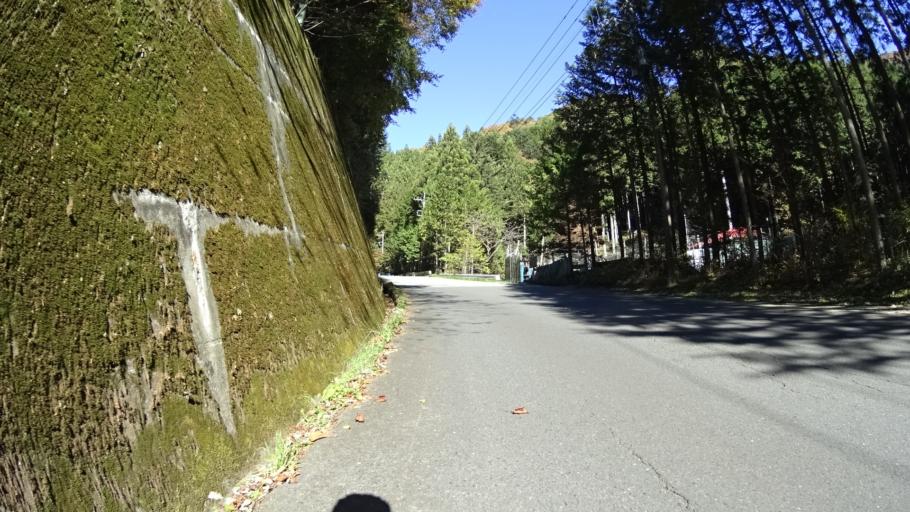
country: JP
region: Yamanashi
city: Otsuki
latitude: 35.7635
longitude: 138.9374
